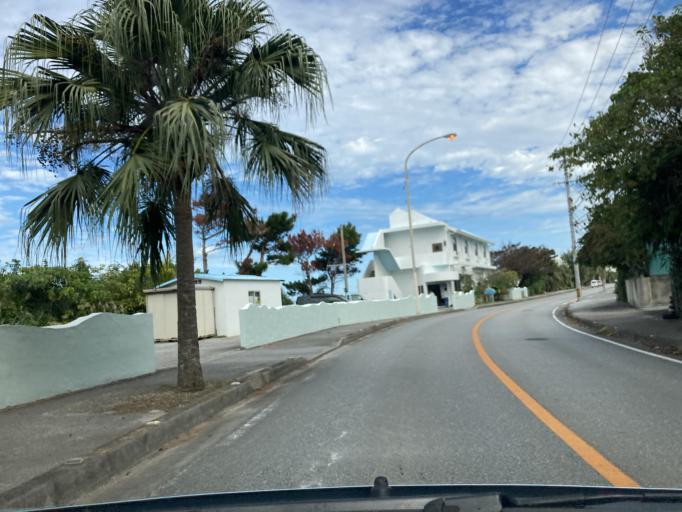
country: JP
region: Okinawa
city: Ishikawa
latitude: 26.4354
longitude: 127.7618
